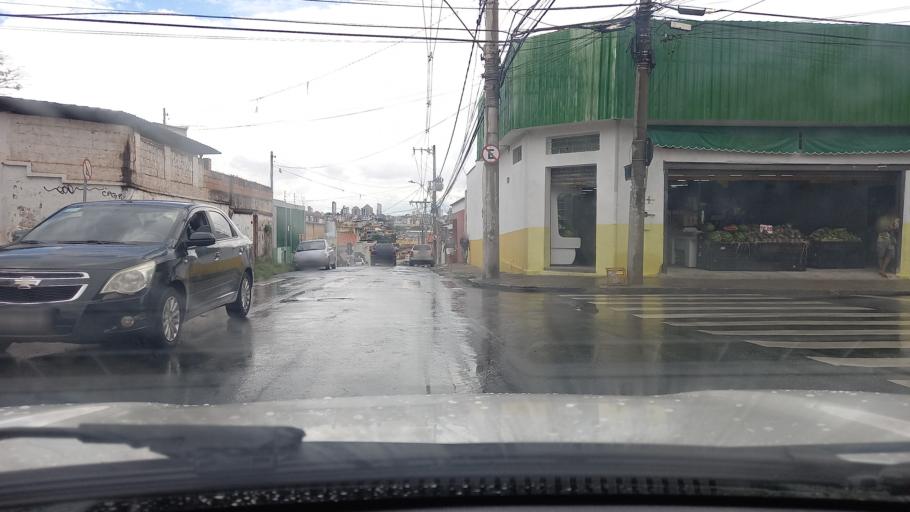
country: BR
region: Minas Gerais
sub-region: Belo Horizonte
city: Belo Horizonte
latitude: -19.9042
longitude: -43.9521
